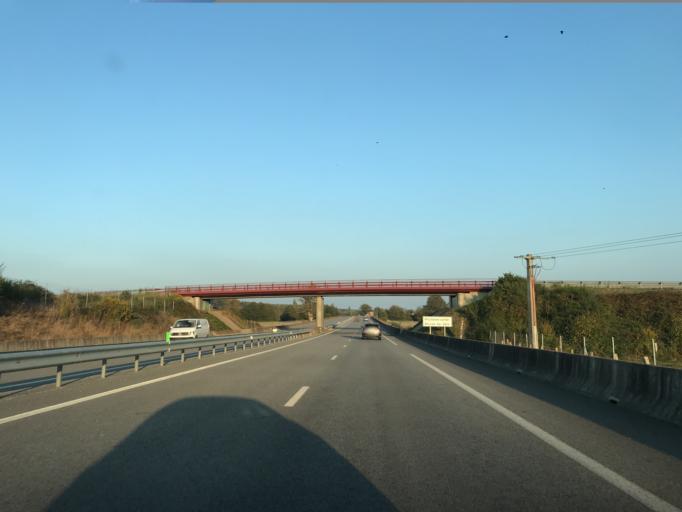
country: FR
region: Lower Normandy
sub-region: Departement de l'Orne
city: Valframbert
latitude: 48.4791
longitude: 0.2188
